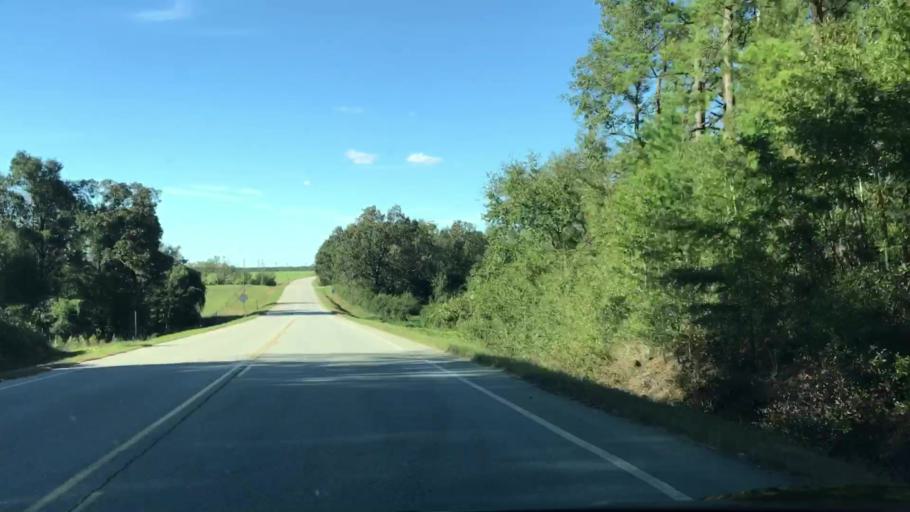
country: US
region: Georgia
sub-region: Jefferson County
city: Louisville
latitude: 33.0714
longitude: -82.4080
